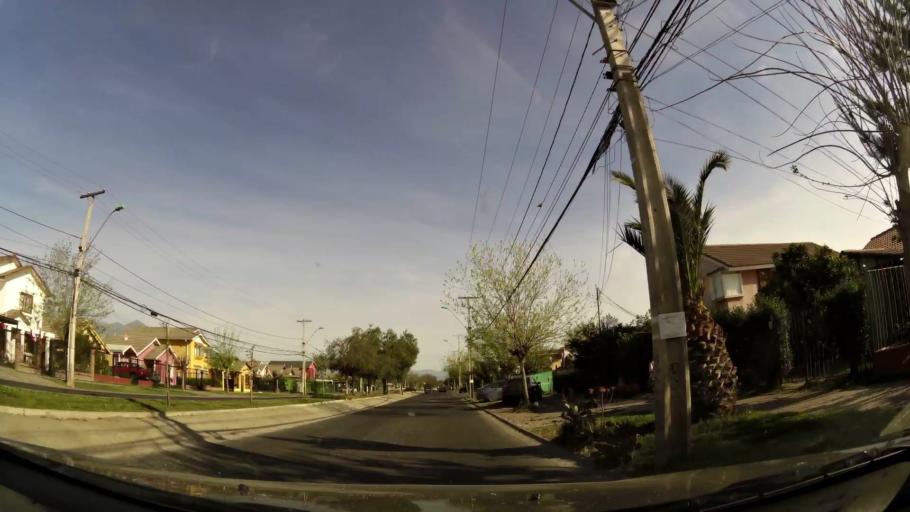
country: CL
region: Santiago Metropolitan
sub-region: Provincia de Cordillera
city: Puente Alto
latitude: -33.5817
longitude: -70.5636
